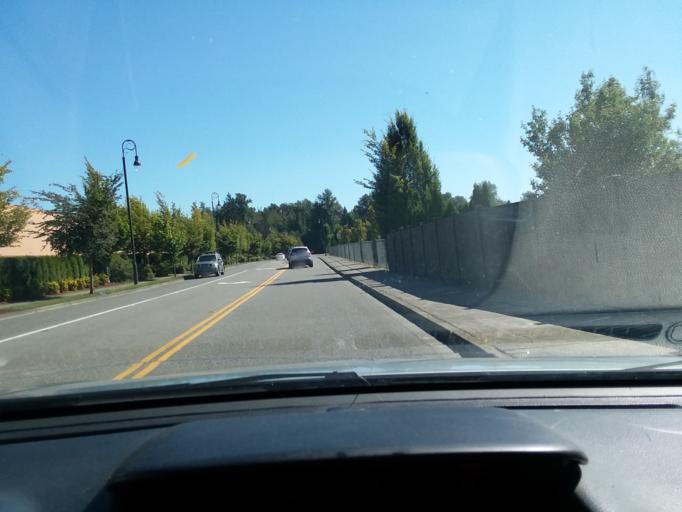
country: US
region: Washington
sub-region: Snohomish County
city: Smokey Point
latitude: 48.1496
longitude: -122.1938
